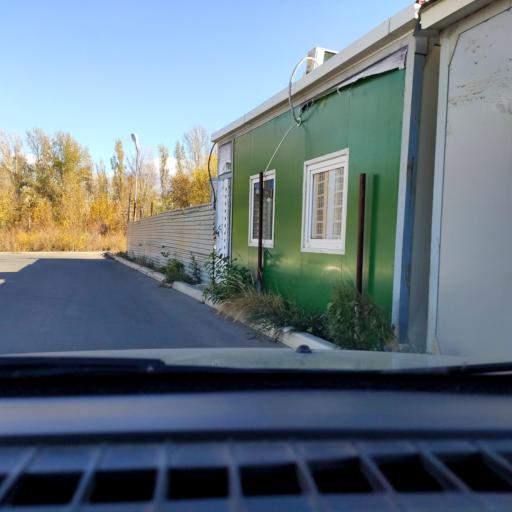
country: RU
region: Samara
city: Tol'yatti
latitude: 53.5122
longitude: 49.2551
